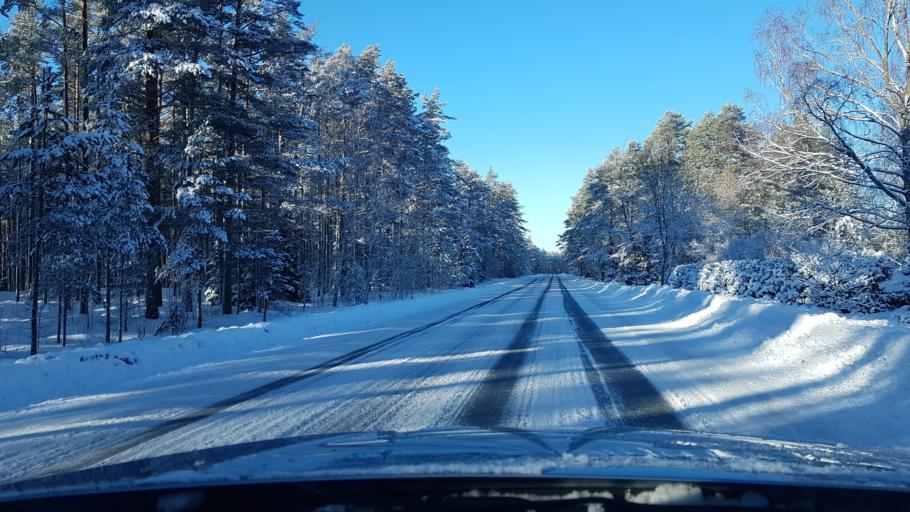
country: EE
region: Hiiumaa
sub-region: Kaerdla linn
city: Kardla
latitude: 58.9238
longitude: 22.7915
